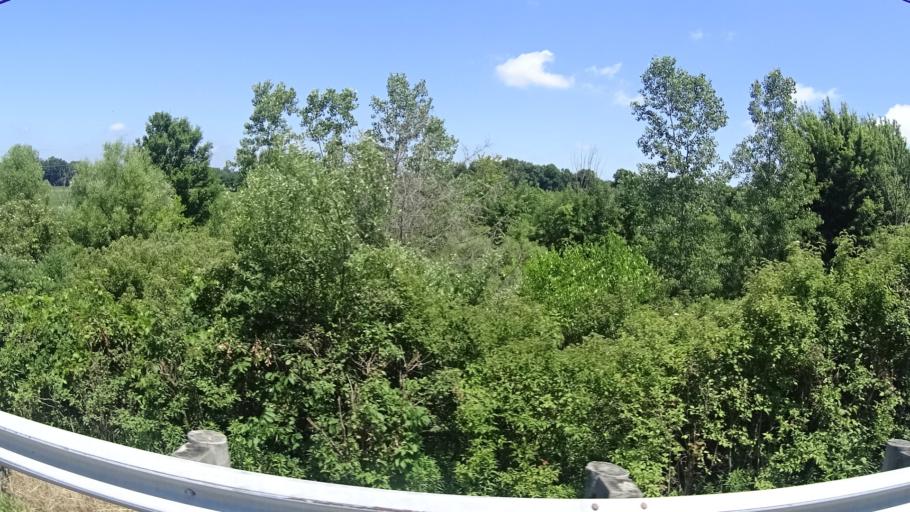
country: US
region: Ohio
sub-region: Huron County
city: Wakeman
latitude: 41.3341
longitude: -82.4175
